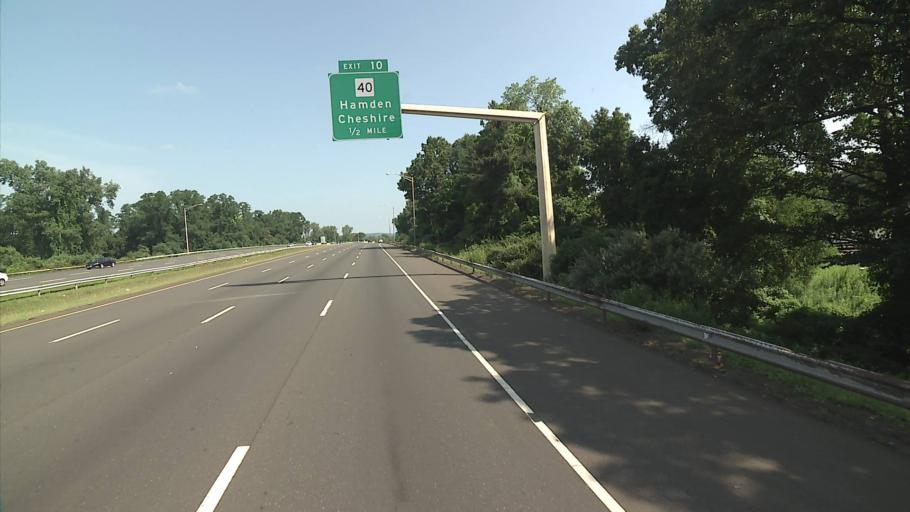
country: US
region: Connecticut
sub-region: New Haven County
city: North Haven
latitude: 41.3649
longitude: -72.8690
